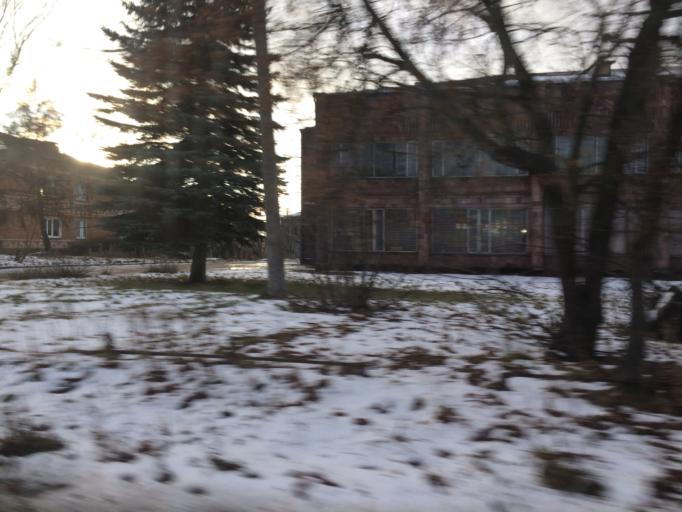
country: RU
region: Tula
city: Cherepet'
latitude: 54.1093
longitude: 36.3281
